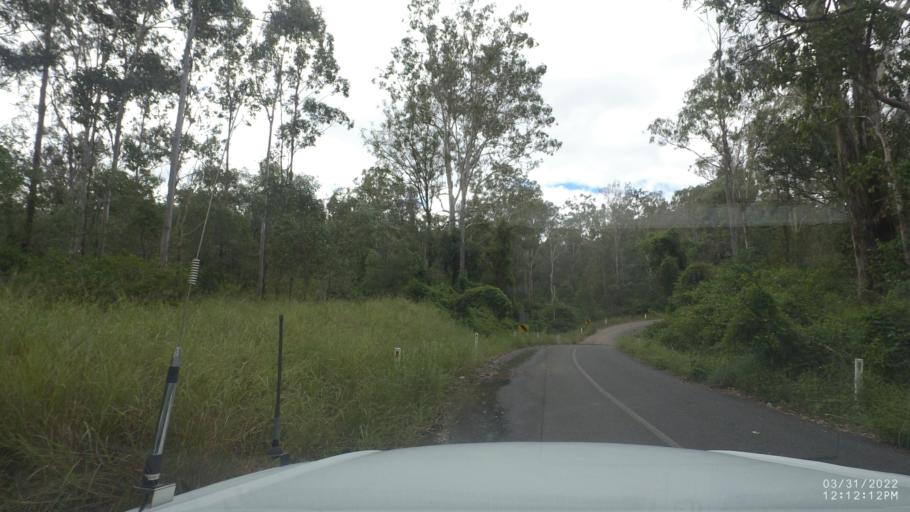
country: AU
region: Queensland
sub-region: Logan
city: Cedar Vale
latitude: -27.9332
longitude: 153.0741
